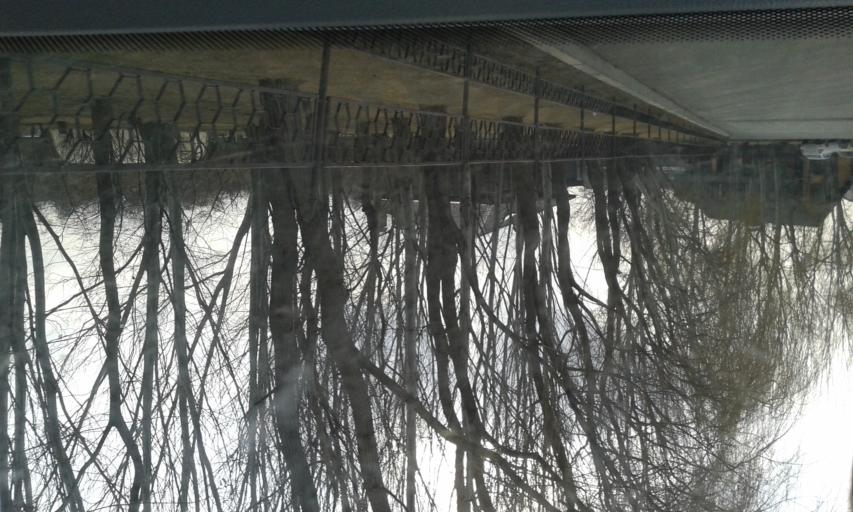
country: RU
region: Volgograd
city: Volgograd
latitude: 48.6564
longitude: 44.4173
